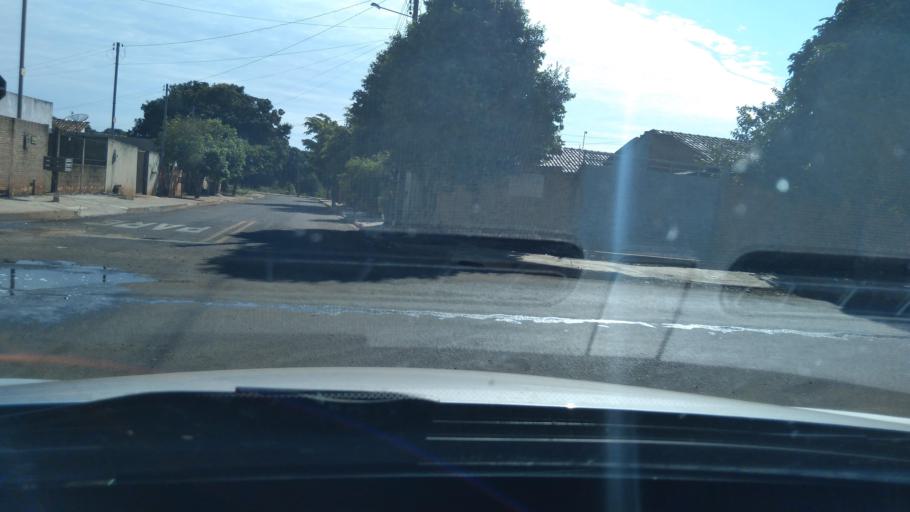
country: BR
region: Goias
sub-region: Mineiros
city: Mineiros
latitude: -17.5353
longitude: -52.5406
